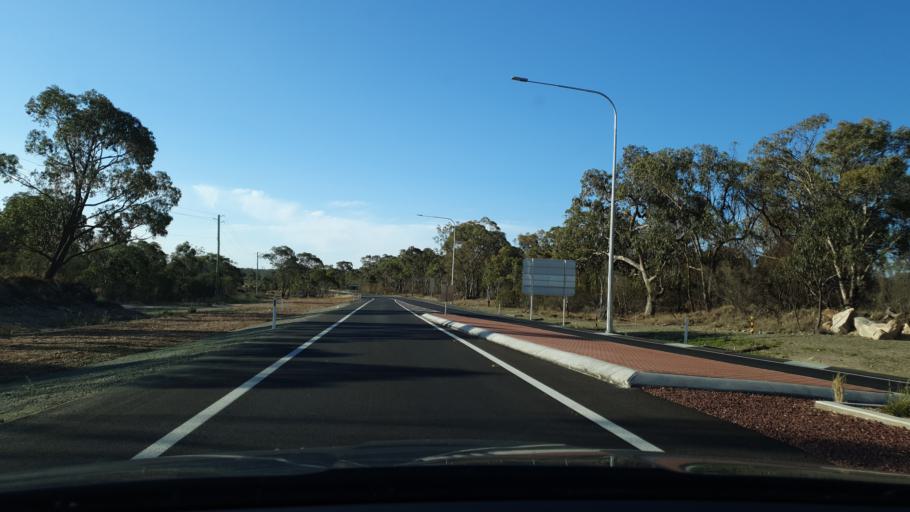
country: AU
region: Queensland
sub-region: Southern Downs
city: Stanthorpe
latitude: -28.6740
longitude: 151.9202
